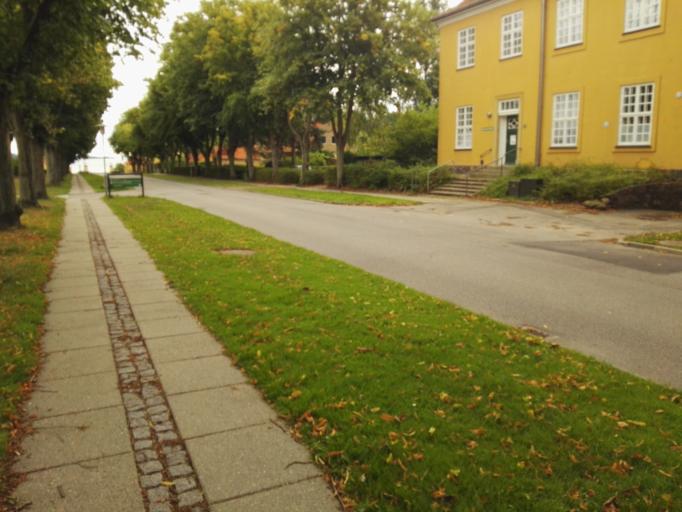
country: DK
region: Zealand
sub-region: Odsherred Kommune
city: Nykobing Sjaelland
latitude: 55.9081
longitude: 11.6651
